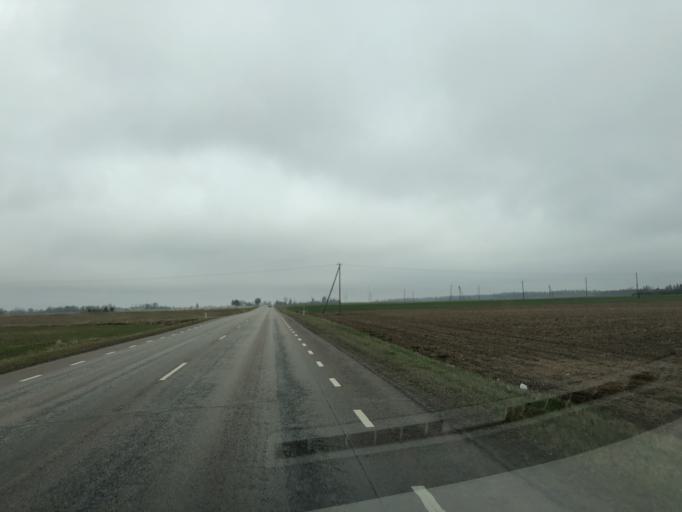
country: EE
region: Laeaene-Virumaa
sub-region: Vaeike-Maarja vald
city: Vaike-Maarja
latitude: 59.1648
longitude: 26.2671
